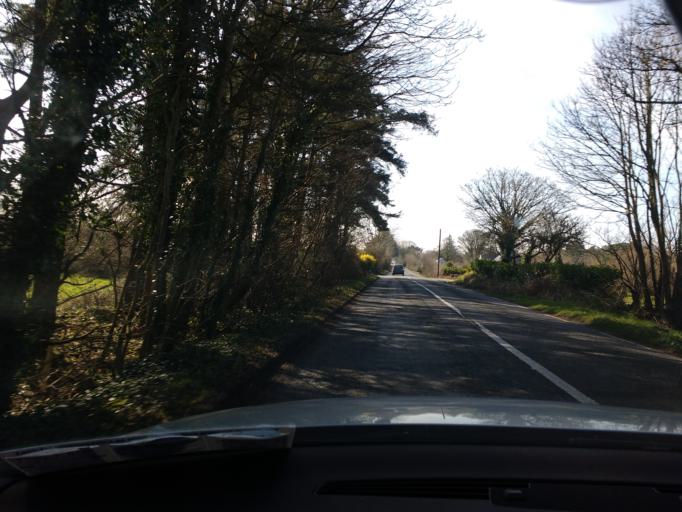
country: IE
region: Munster
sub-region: County Limerick
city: Castleconnell
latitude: 52.6824
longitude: -8.4943
